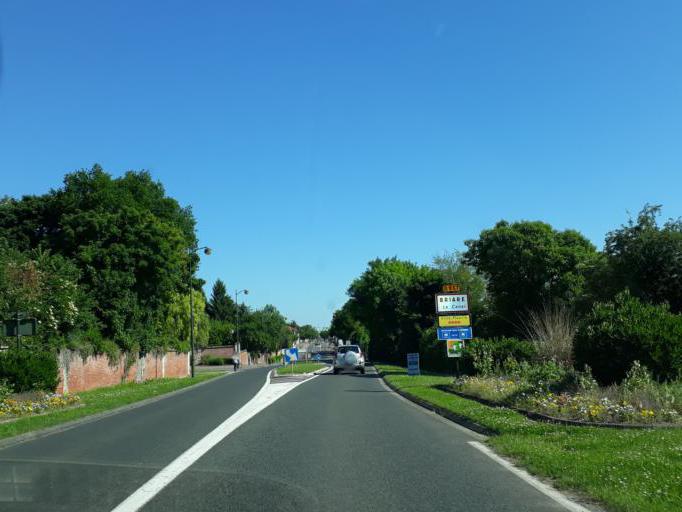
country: FR
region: Centre
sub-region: Departement du Loiret
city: Briare
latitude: 47.6538
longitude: 2.7224
